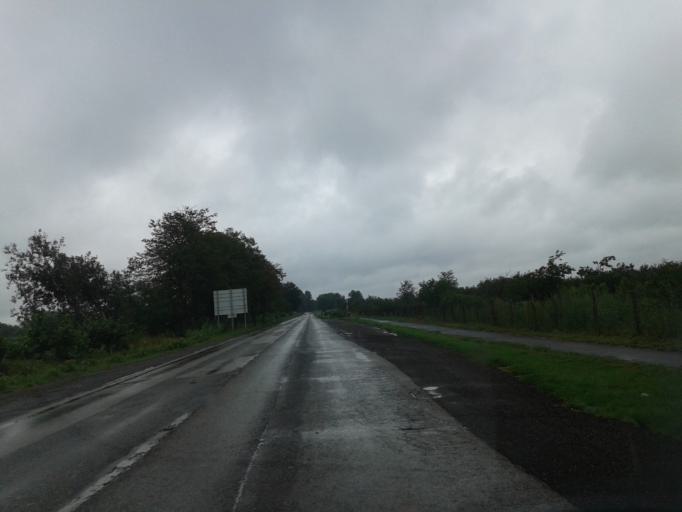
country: HU
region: Bacs-Kiskun
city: Soltvadkert
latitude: 46.5858
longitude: 19.3523
